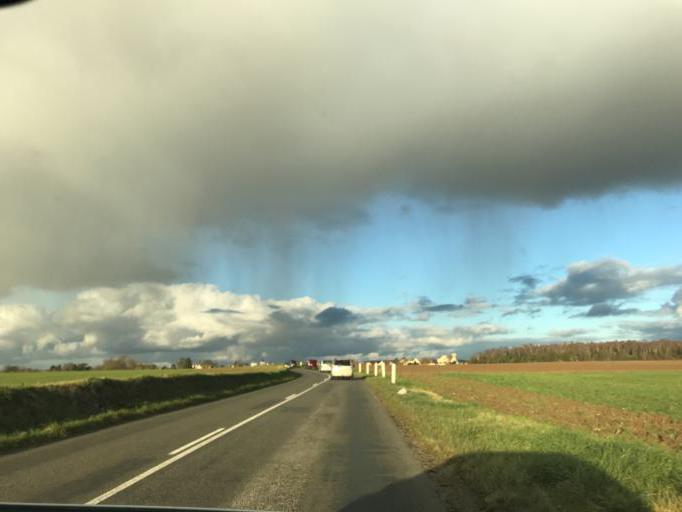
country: FR
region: Ile-de-France
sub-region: Departement de Seine-et-Marne
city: Claye-Souilly
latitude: 48.9591
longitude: 2.6980
